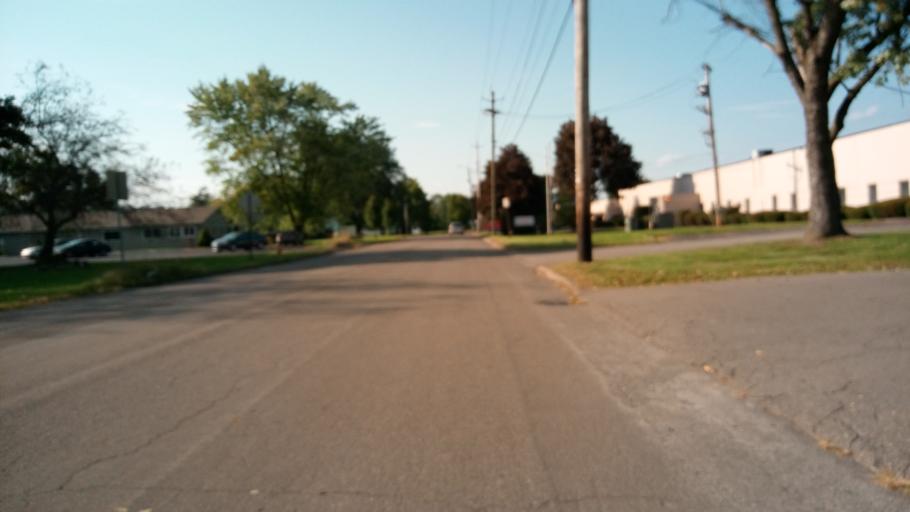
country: US
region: New York
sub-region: Chemung County
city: Elmira
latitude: 42.1086
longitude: -76.8020
